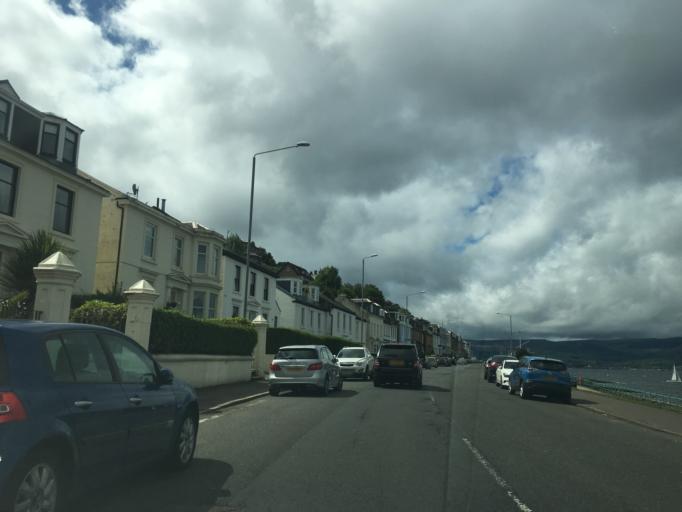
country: GB
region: Scotland
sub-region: Inverclyde
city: Gourock
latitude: 55.9553
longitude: -4.8308
